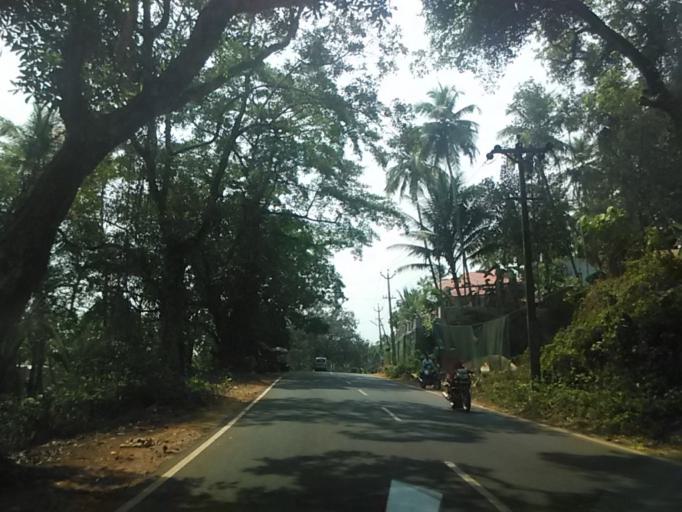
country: IN
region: Kerala
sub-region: Kozhikode
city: Naduvannur
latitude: 11.5115
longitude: 75.7747
